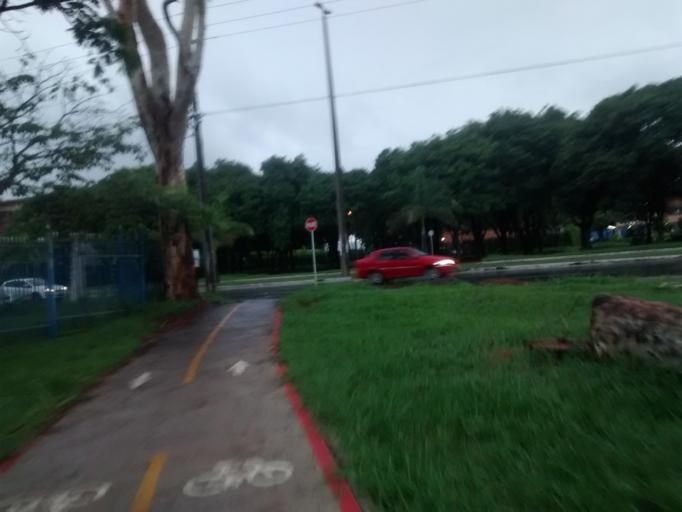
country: BR
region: Federal District
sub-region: Brasilia
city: Brasilia
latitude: -15.7627
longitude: -47.8766
